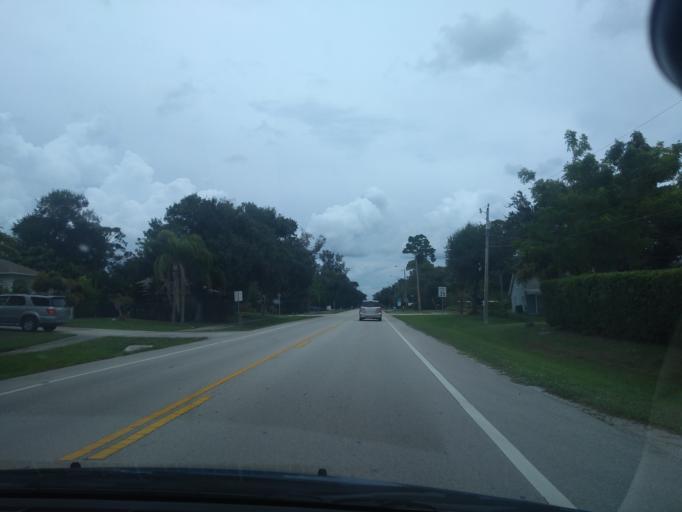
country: US
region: Florida
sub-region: Indian River County
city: Vero Beach South
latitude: 27.6265
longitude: -80.4138
